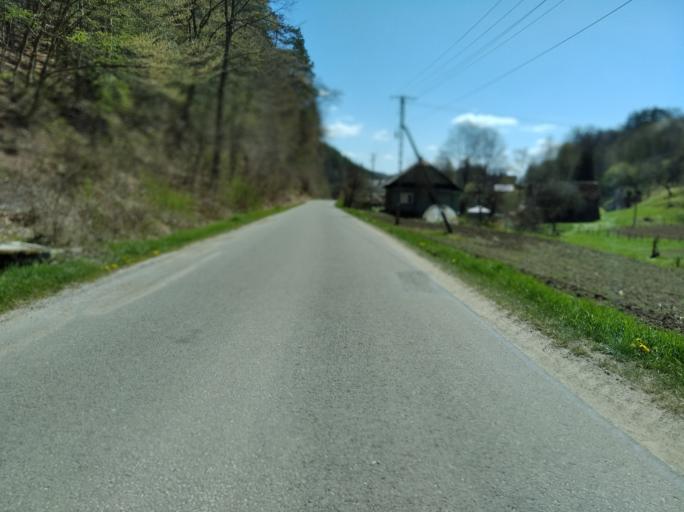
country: PL
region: Subcarpathian Voivodeship
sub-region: Powiat brzozowski
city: Dydnia
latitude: 49.7144
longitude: 22.1915
